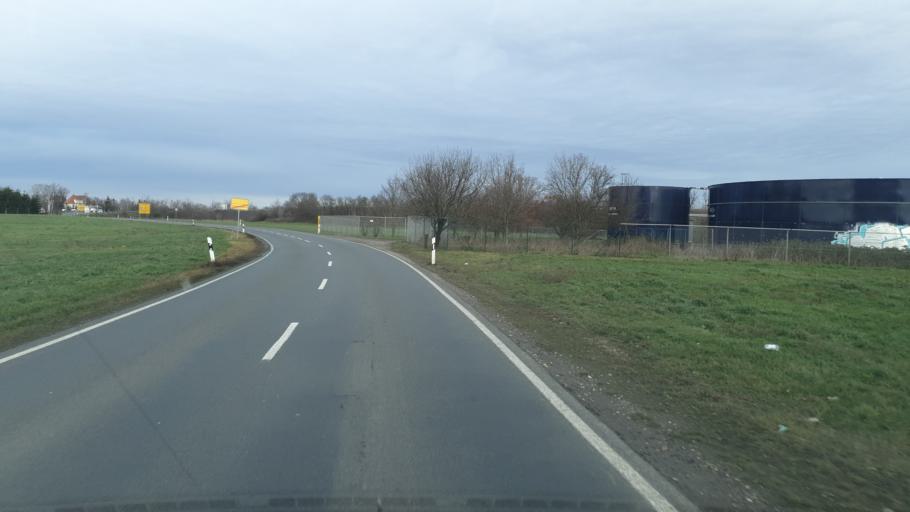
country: DE
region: Saxony
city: Kitzen
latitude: 51.2504
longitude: 12.2754
